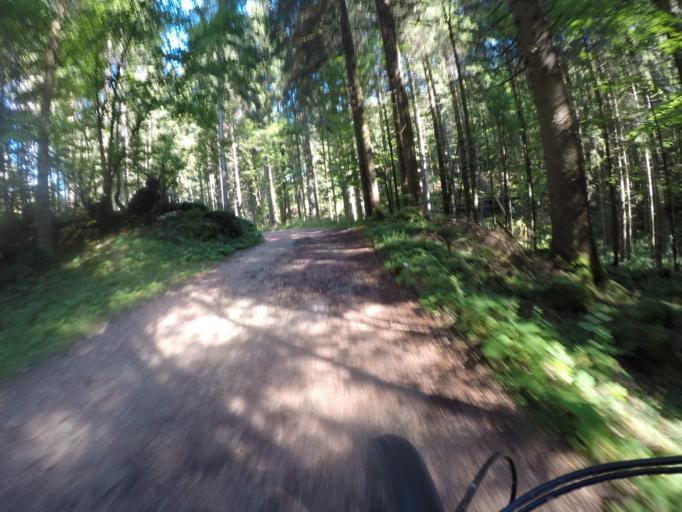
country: IT
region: Veneto
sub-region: Provincia di Vicenza
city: Canove di Roana
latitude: 45.8343
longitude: 11.5028
